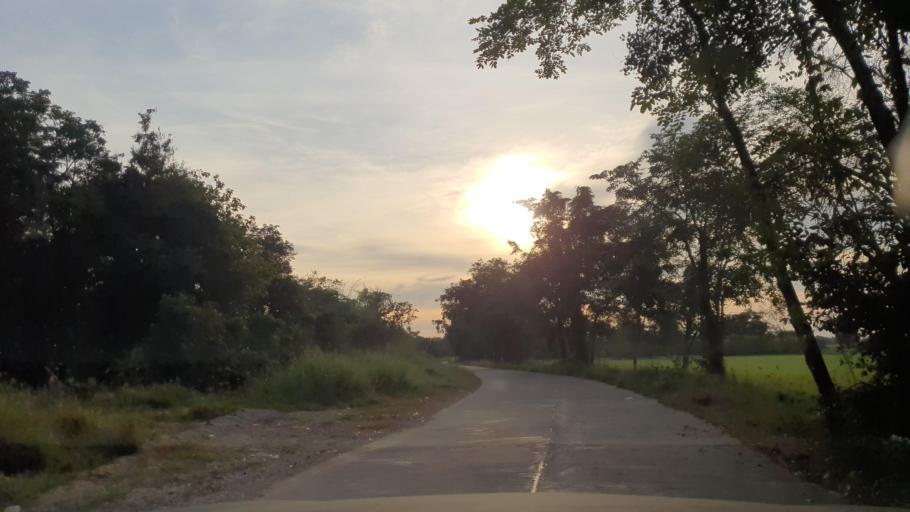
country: TH
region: Nakhon Sawan
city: Krok Phra
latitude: 15.6626
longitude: 100.0153
